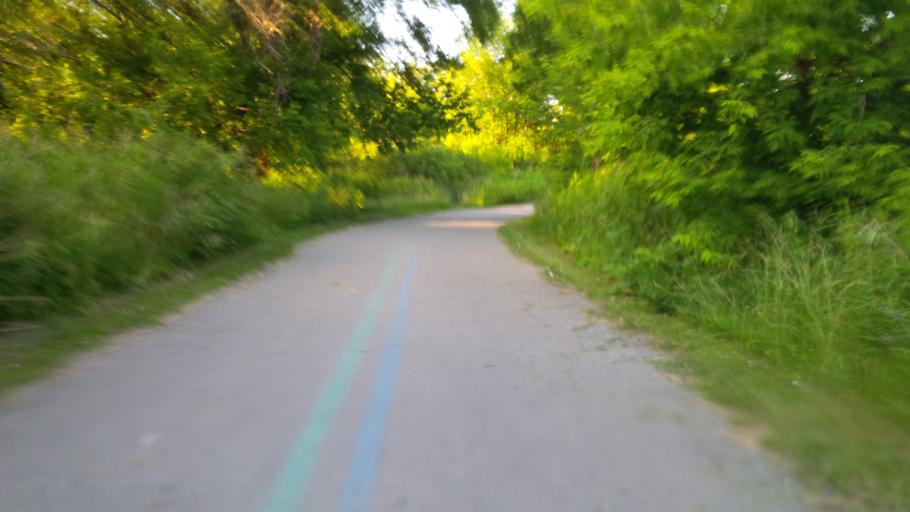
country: CA
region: Ontario
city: Toronto
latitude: 43.6429
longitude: -79.3362
